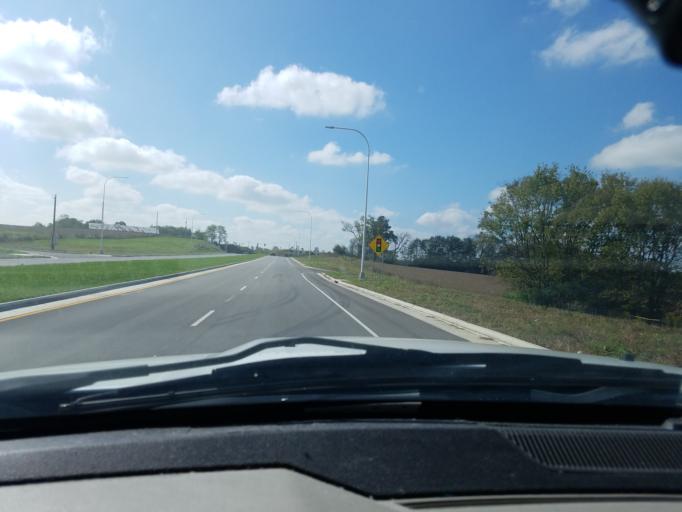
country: US
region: Kentucky
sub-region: Scott County
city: Georgetown
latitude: 38.2406
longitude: -84.5504
